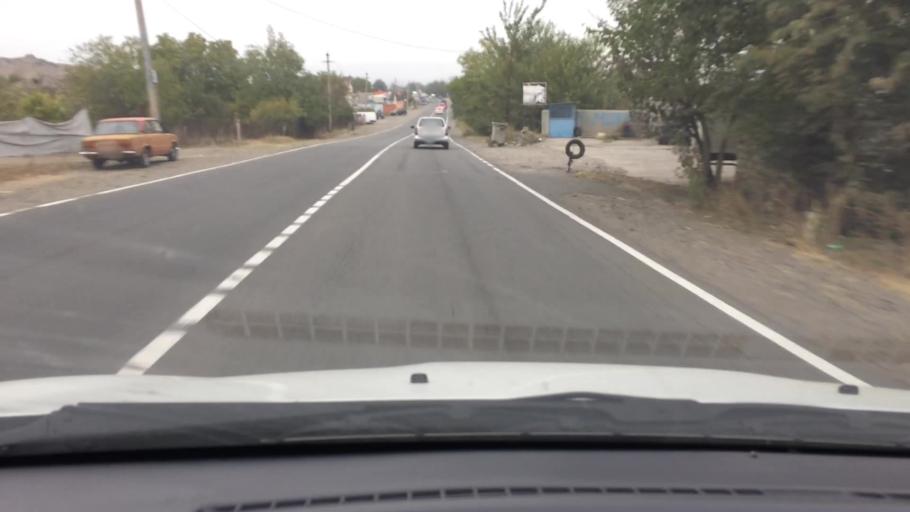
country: GE
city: Naghvarevi
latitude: 41.3730
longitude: 44.8353
